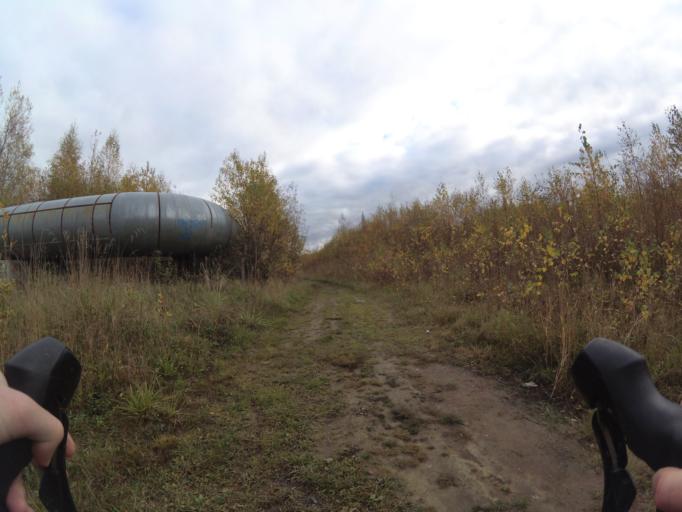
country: RU
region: St.-Petersburg
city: Lakhtinskiy
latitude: 60.0036
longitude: 30.1505
